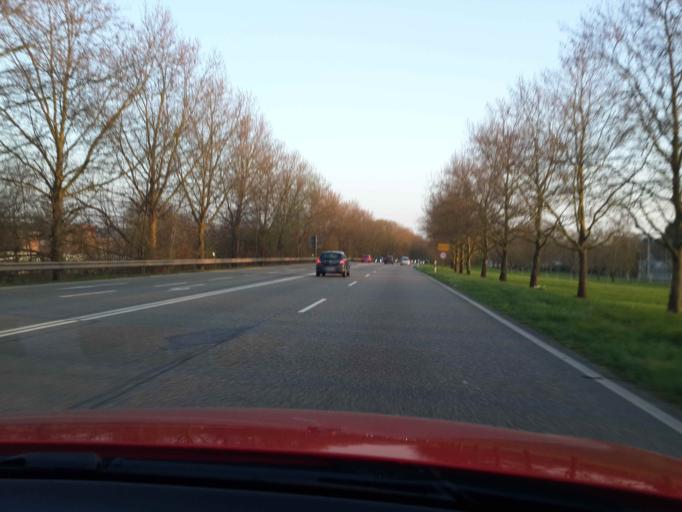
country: DE
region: Baden-Wuerttemberg
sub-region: Regierungsbezirk Stuttgart
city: Neckarsulm
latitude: 49.1755
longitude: 9.2026
